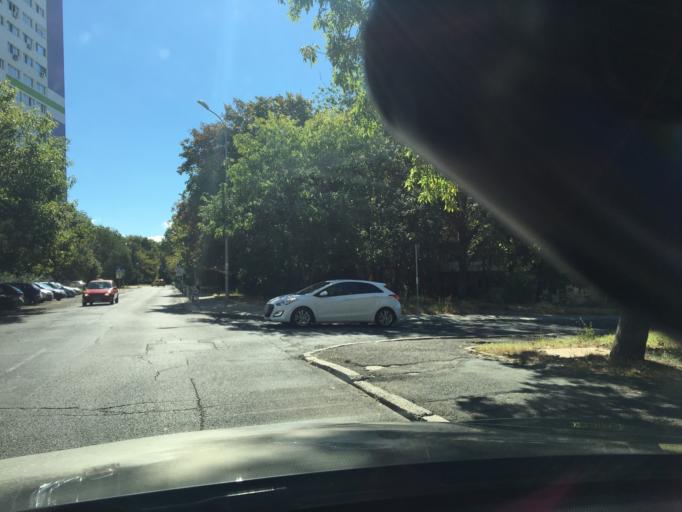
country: BG
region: Burgas
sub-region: Obshtina Burgas
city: Burgas
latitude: 42.5157
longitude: 27.4582
